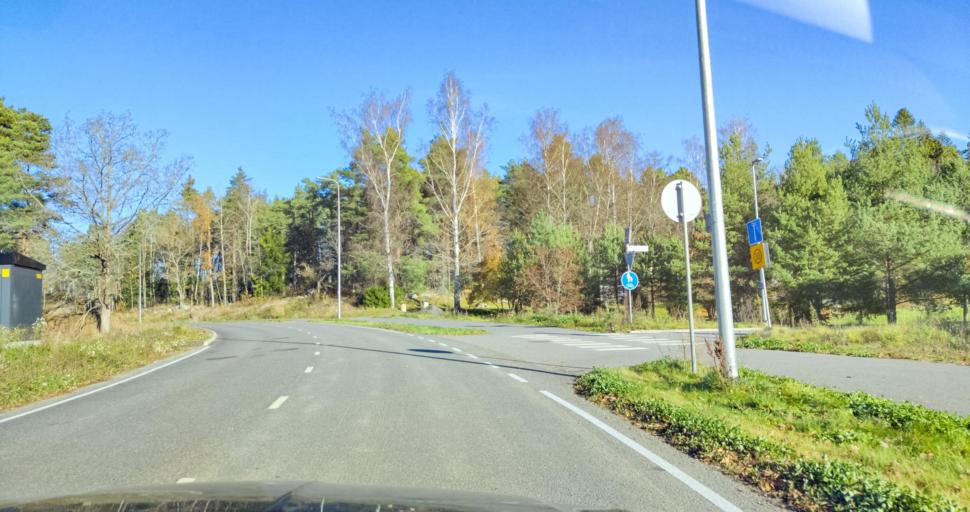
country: FI
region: Varsinais-Suomi
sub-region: Turku
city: Turku
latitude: 60.4081
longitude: 22.2105
